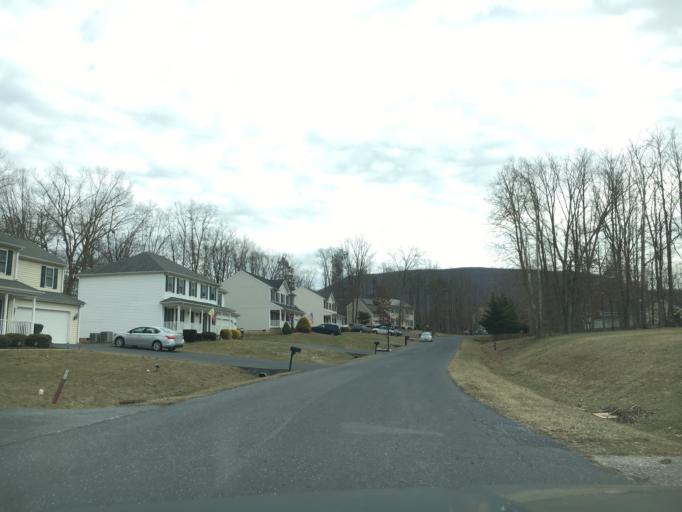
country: US
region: Virginia
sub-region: Augusta County
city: Crimora
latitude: 38.1389
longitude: -78.8406
